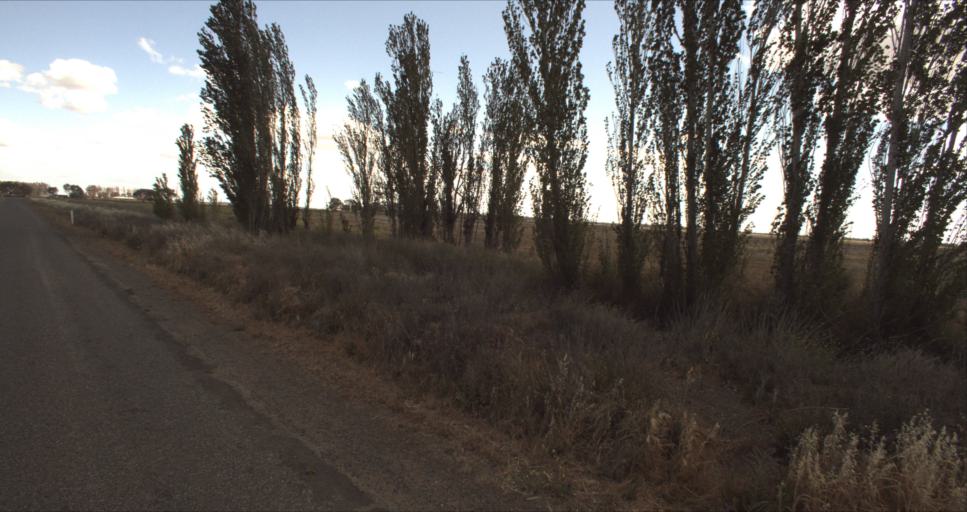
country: AU
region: New South Wales
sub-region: Leeton
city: Leeton
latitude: -34.5275
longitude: 146.2202
